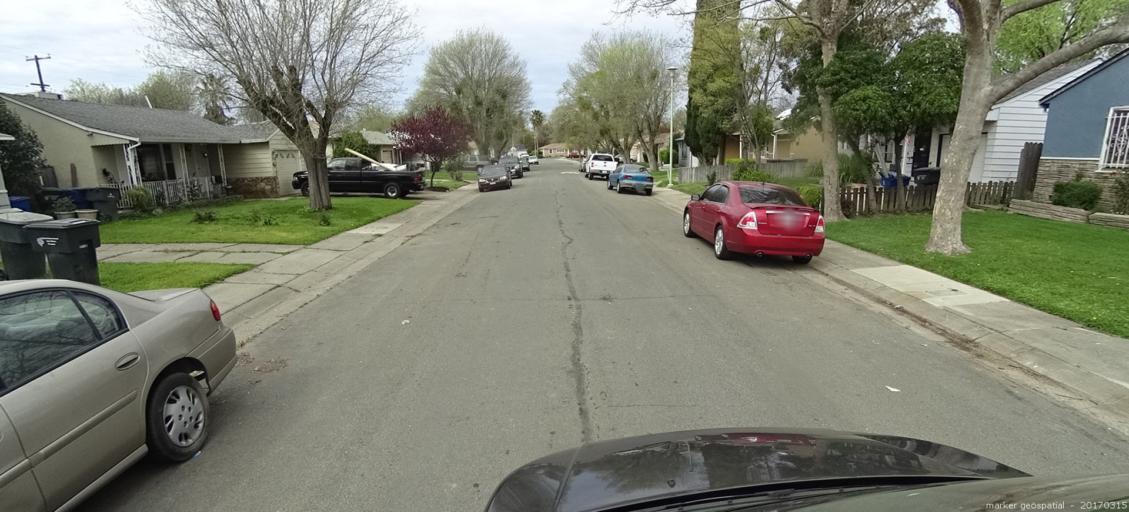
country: US
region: California
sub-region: Sacramento County
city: Parkway
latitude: 38.5200
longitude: -121.5029
